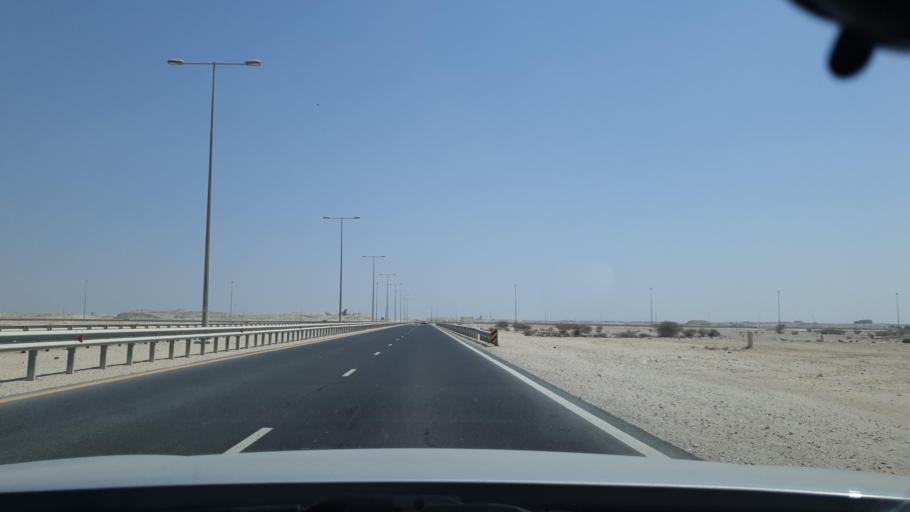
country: QA
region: Baladiyat Umm Salal
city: Umm Salal Muhammad
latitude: 25.3866
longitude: 51.3570
